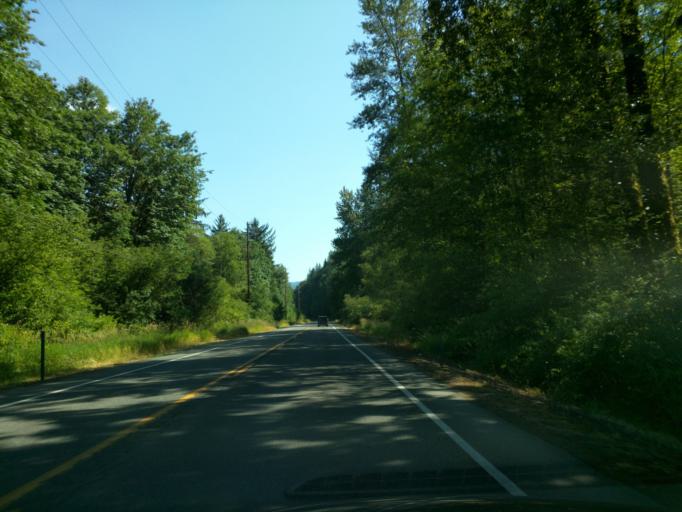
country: US
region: Washington
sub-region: Whatcom County
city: Peaceful Valley
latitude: 48.8781
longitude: -122.1573
